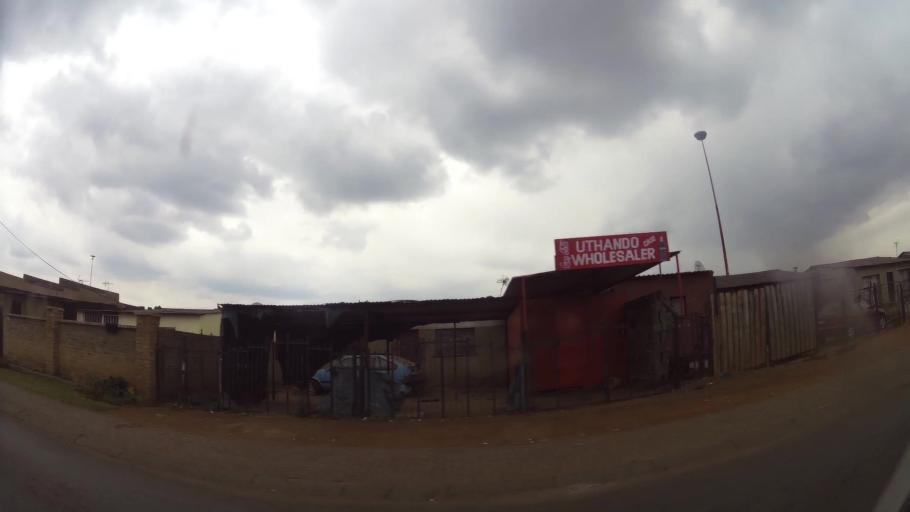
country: ZA
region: Gauteng
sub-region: Ekurhuleni Metropolitan Municipality
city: Germiston
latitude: -26.3411
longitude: 28.1497
